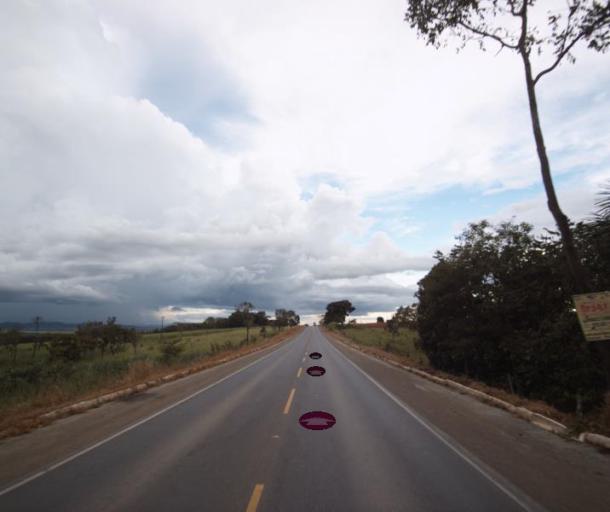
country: BR
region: Goias
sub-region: Itapaci
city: Itapaci
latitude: -14.8415
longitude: -49.3110
